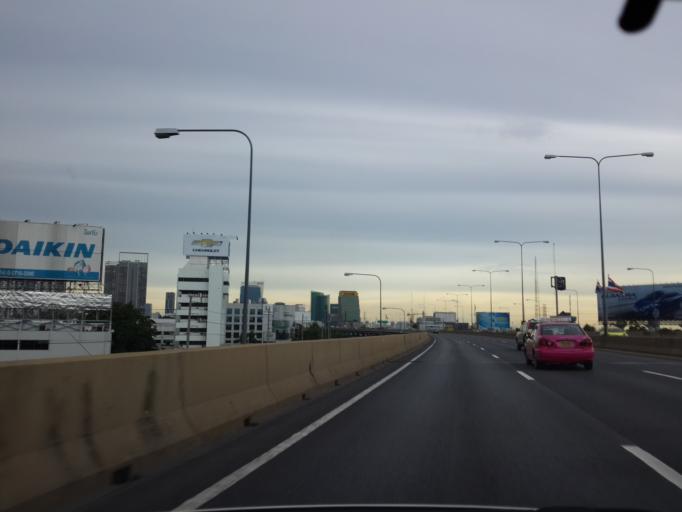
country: TH
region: Bangkok
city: Chatuchak
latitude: 13.8396
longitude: 100.5578
